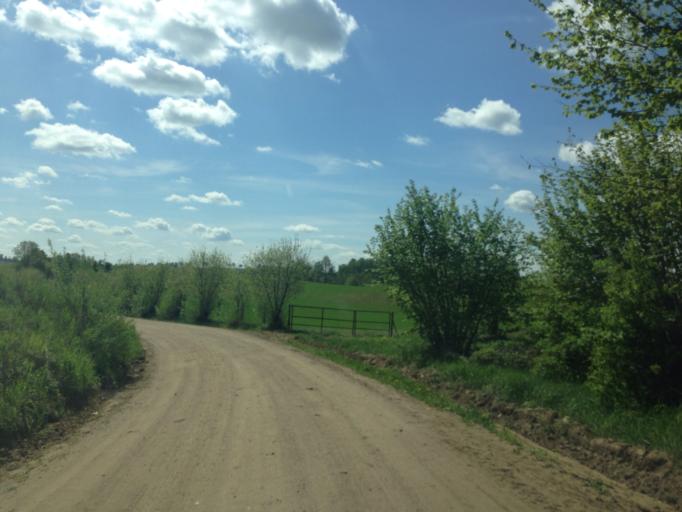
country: PL
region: Kujawsko-Pomorskie
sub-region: Powiat brodnicki
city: Brzozie
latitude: 53.3153
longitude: 19.6304
